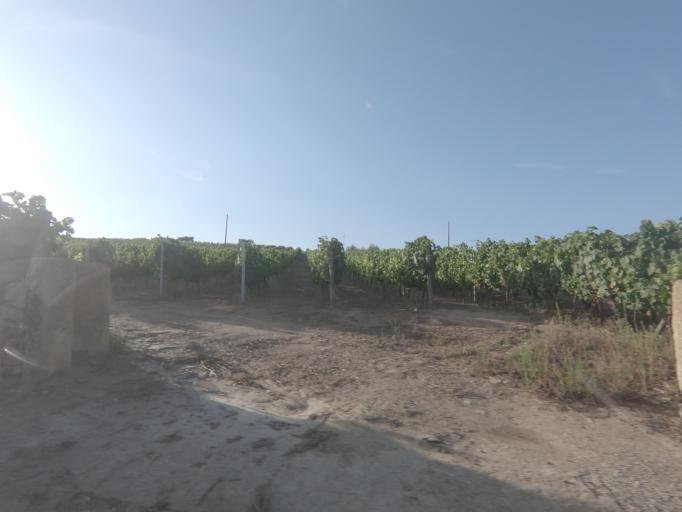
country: PT
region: Vila Real
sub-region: Sabrosa
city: Sabrosa
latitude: 41.2722
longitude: -7.5187
